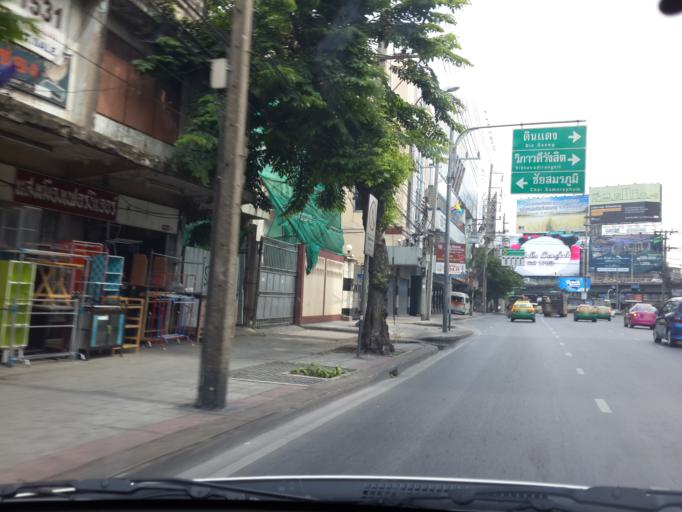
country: TH
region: Bangkok
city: Ratchathewi
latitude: 13.7615
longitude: 100.5425
